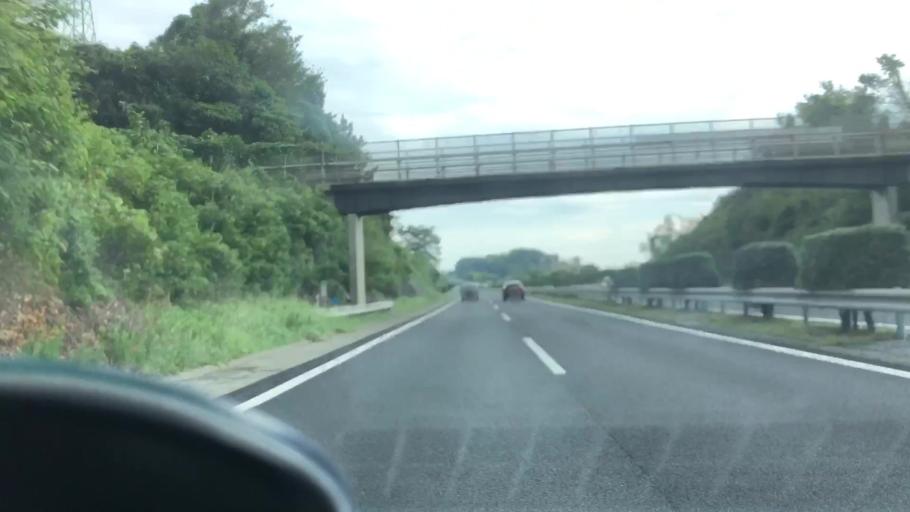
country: JP
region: Hyogo
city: Yashiro
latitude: 34.9372
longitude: 134.8824
